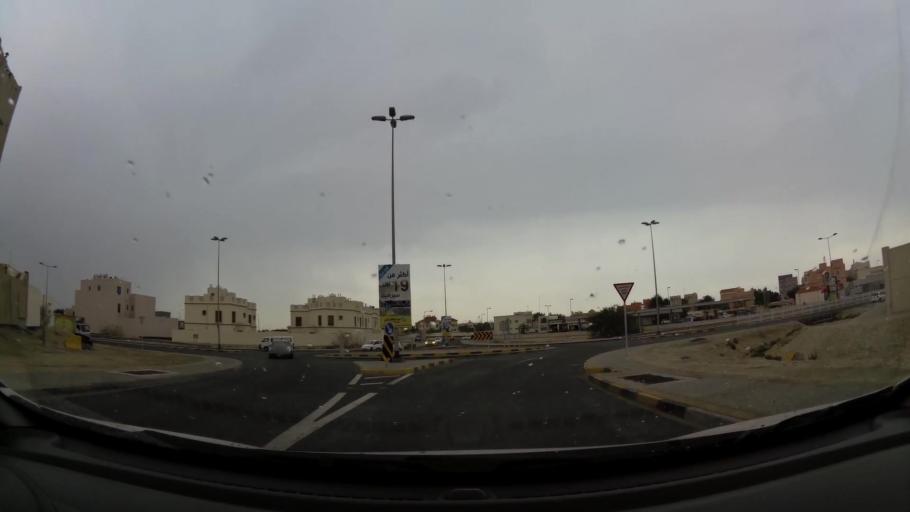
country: BH
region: Central Governorate
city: Madinat Hamad
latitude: 26.1321
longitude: 50.4938
